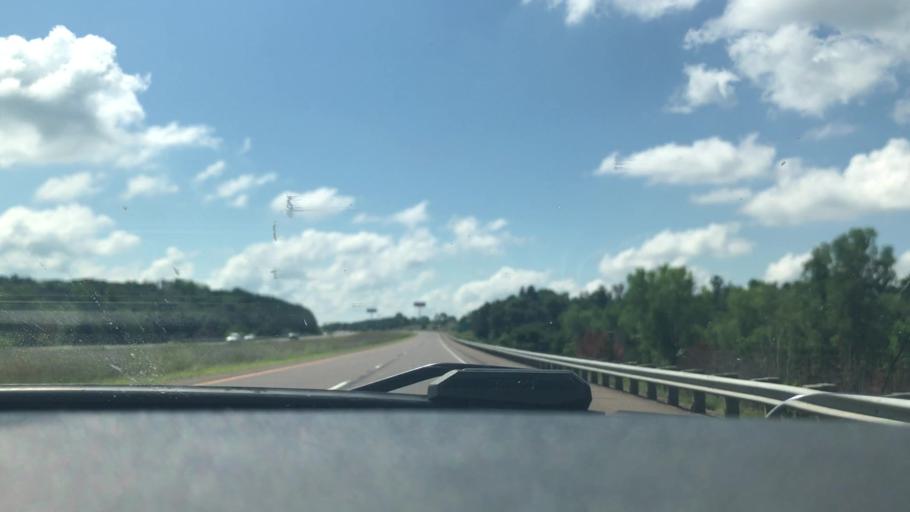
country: US
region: Wisconsin
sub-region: Chippewa County
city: Lake Hallie
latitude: 44.9108
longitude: -91.4282
